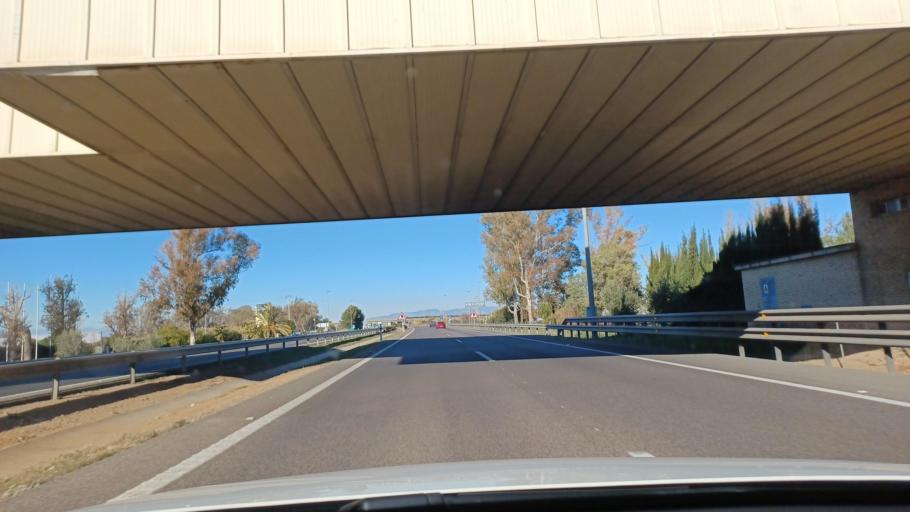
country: ES
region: Valencia
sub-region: Provincia de Castello
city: Alquerias del Nino Perdido
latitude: 39.8646
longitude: -0.1220
